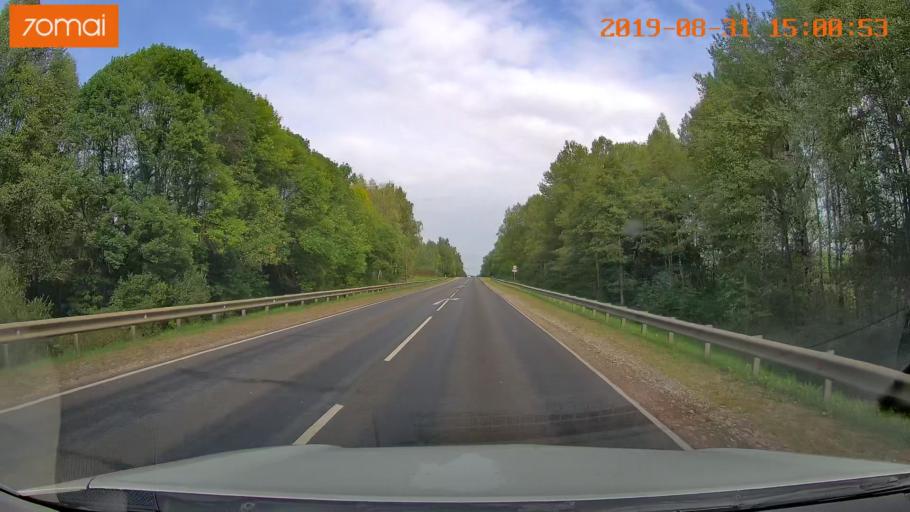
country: RU
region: Kaluga
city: Spas-Demensk
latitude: 54.3353
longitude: 34.0428
